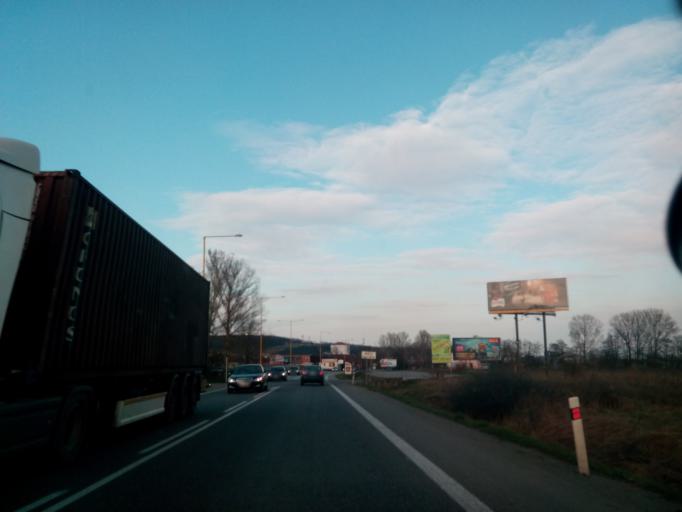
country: SK
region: Kosicky
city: Kosice
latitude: 48.6271
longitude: 21.1625
